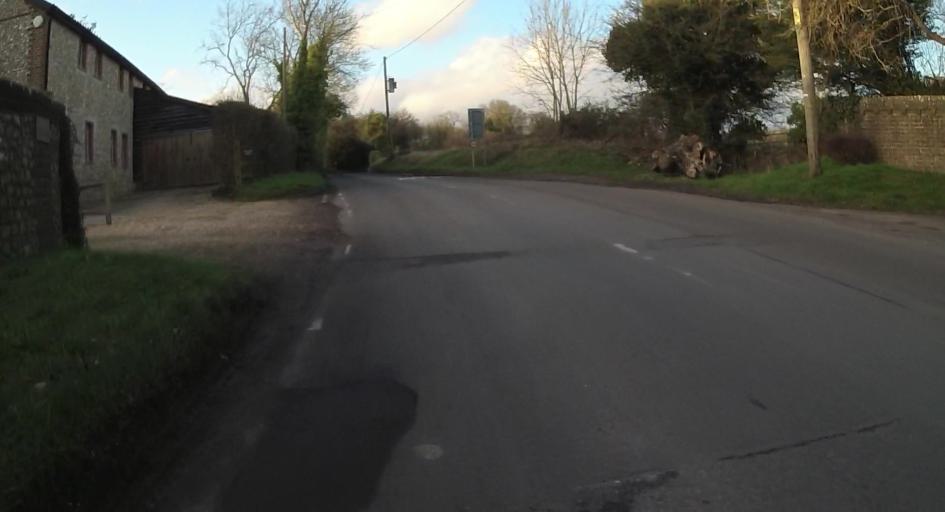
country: GB
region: England
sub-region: Hampshire
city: Four Marks
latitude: 51.1220
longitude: -1.0625
